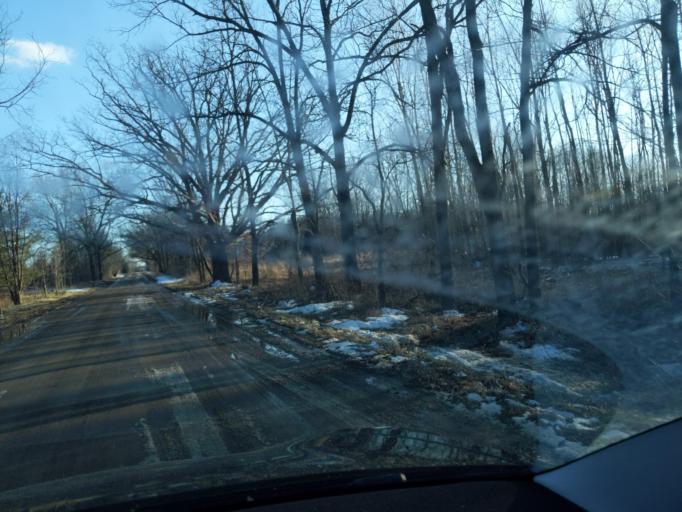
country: US
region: Michigan
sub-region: Ingham County
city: Stockbridge
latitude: 42.5078
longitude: -84.2416
